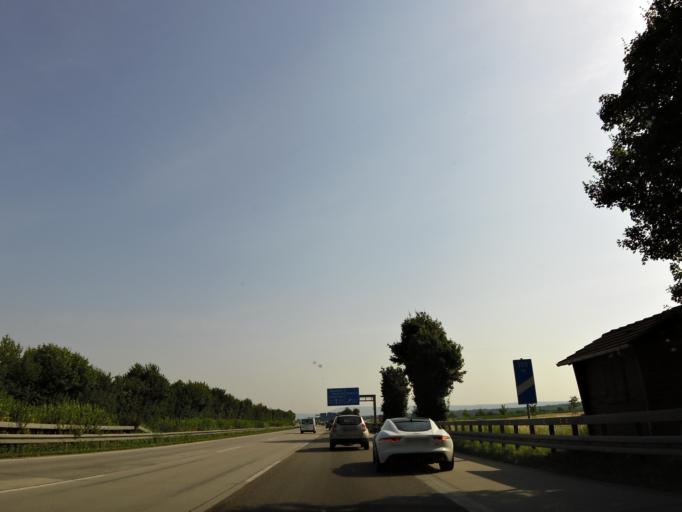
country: DE
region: Baden-Wuerttemberg
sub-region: Karlsruhe Region
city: Sankt Leon-Rot
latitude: 49.2706
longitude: 8.6138
